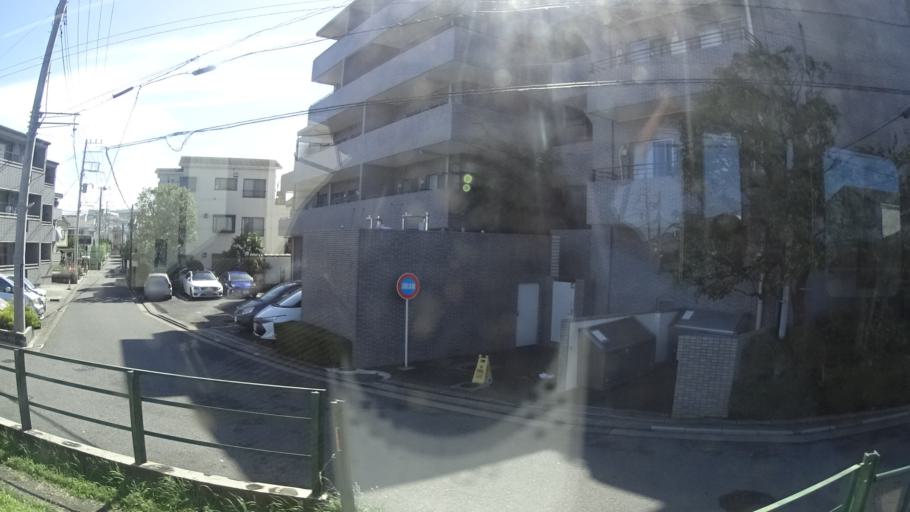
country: JP
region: Kanagawa
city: Fujisawa
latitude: 35.3298
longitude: 139.4852
